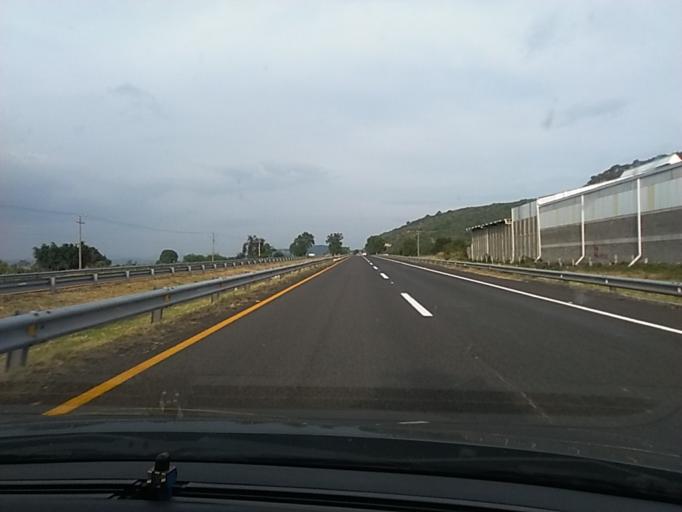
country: MX
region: Michoacan
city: Copandaro de Galeana
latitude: 19.8829
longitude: -101.1968
